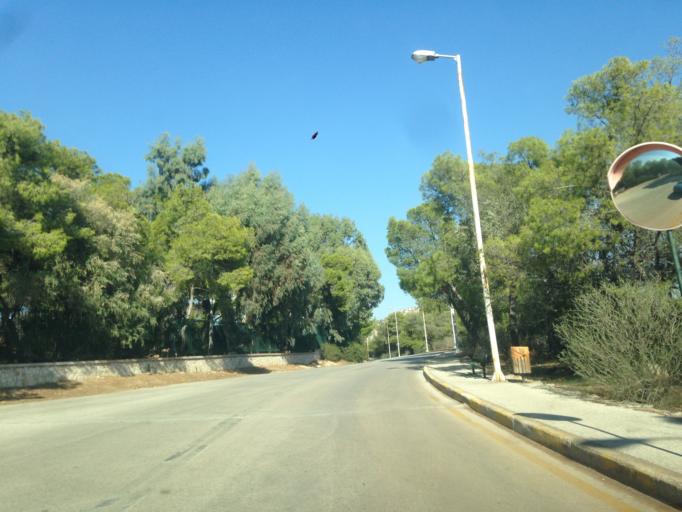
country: GR
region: Attica
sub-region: Nomarchia Anatolikis Attikis
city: Vouliagmeni
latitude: 37.8045
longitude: 23.7722
